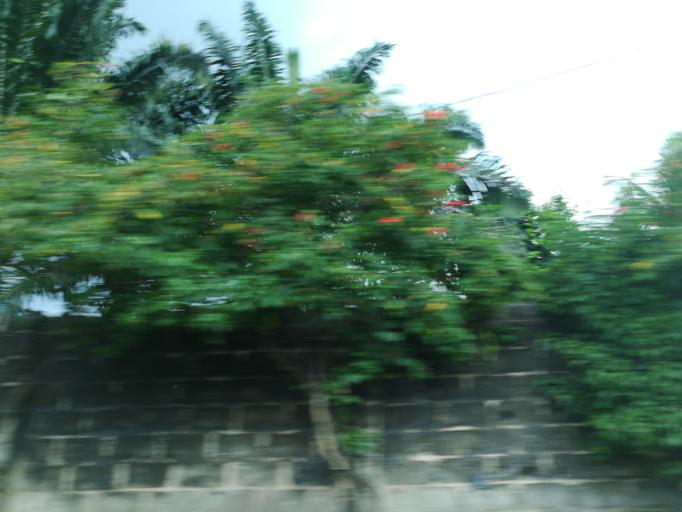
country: NG
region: Rivers
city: Port Harcourt
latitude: 4.8195
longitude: 7.0670
